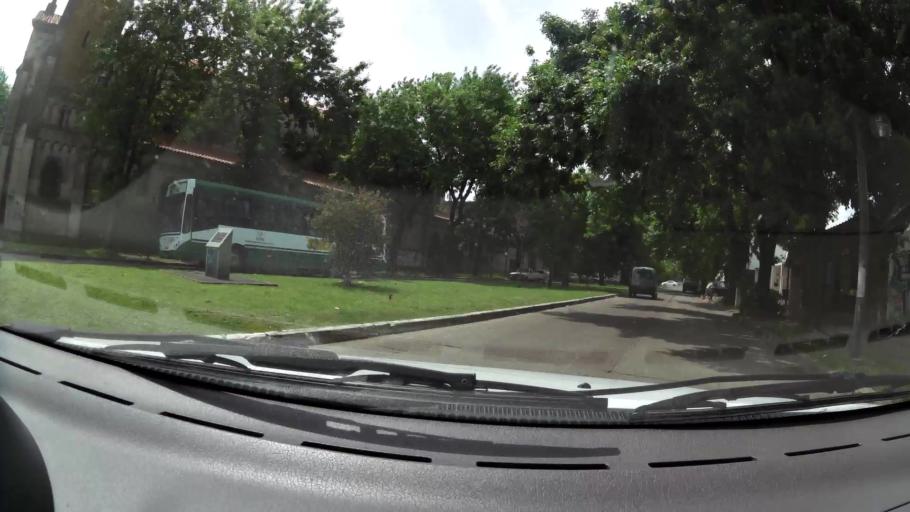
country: AR
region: Buenos Aires
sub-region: Partido de La Plata
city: La Plata
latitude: -34.9418
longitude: -57.9521
